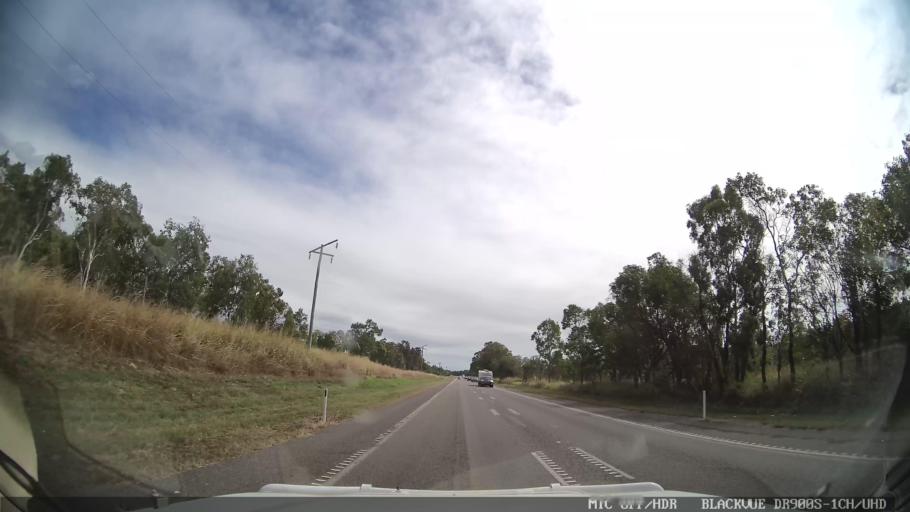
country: AU
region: Queensland
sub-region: Hinchinbrook
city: Ingham
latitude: -19.0051
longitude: 146.3590
